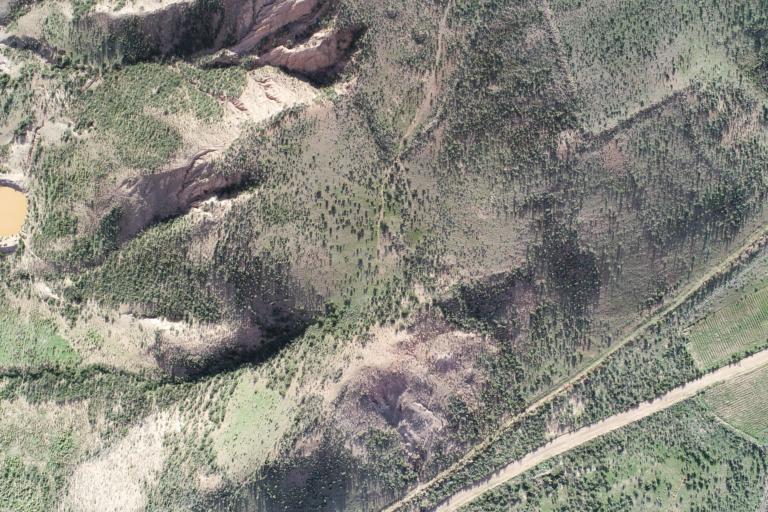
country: BO
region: La Paz
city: Curahuara de Carangas
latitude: -17.2996
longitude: -68.4907
